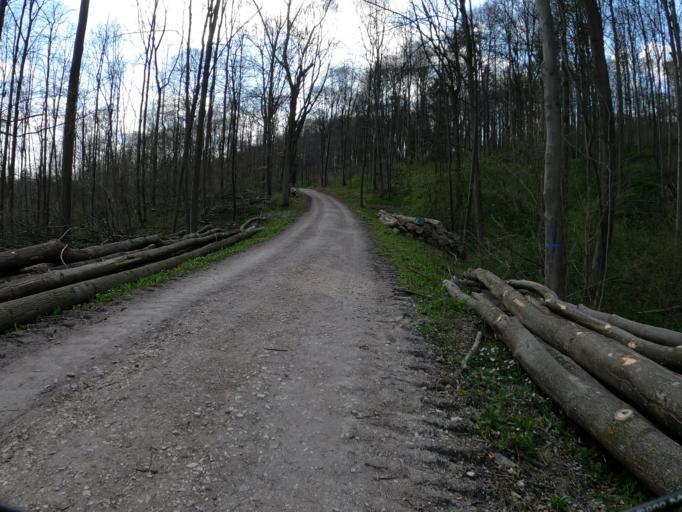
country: DE
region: Bavaria
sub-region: Swabia
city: Neu-Ulm
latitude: 48.4291
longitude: 10.0339
